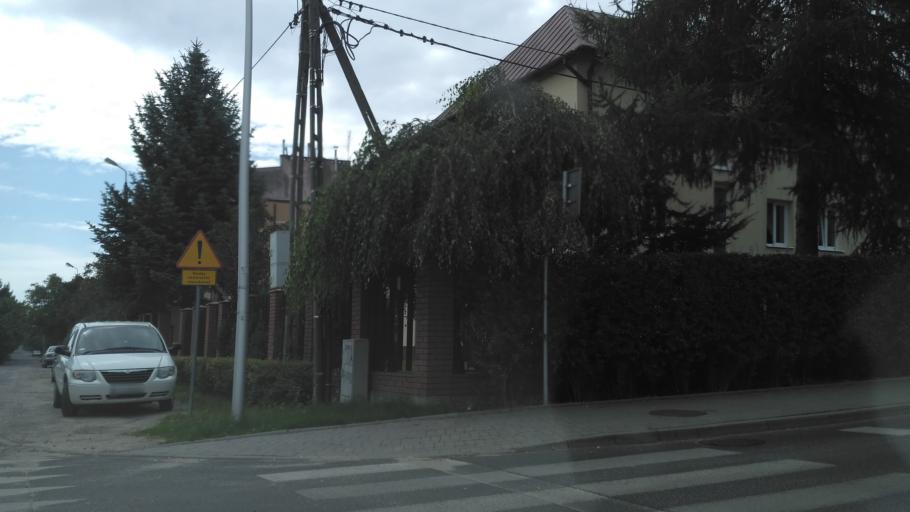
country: PL
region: Lublin Voivodeship
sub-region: Powiat lubelski
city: Lublin
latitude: 51.2165
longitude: 22.5838
